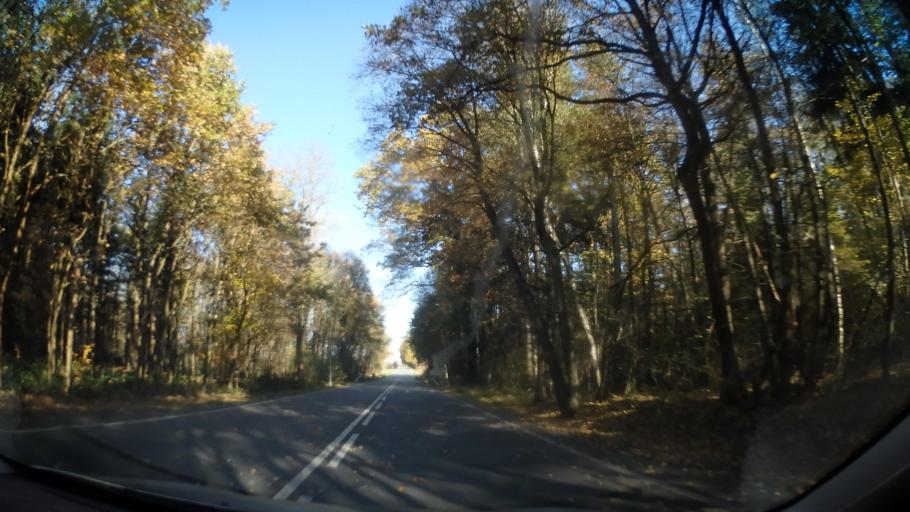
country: CZ
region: Kralovehradecky
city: Trebechovice pod Orebem
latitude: 50.2127
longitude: 16.0335
